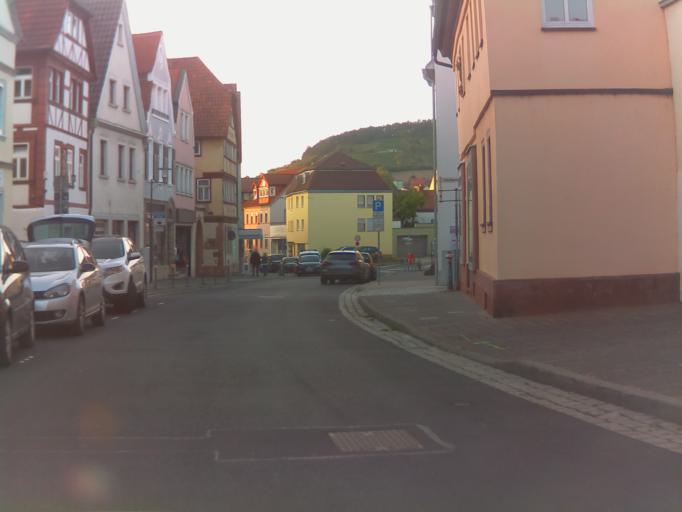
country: DE
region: Bavaria
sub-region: Regierungsbezirk Unterfranken
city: Hammelburg
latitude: 50.1165
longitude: 9.8889
